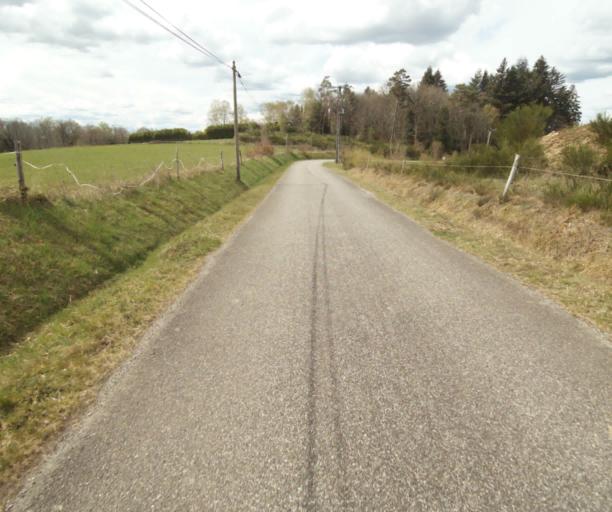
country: FR
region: Limousin
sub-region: Departement de la Correze
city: Laguenne
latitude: 45.2295
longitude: 1.8739
